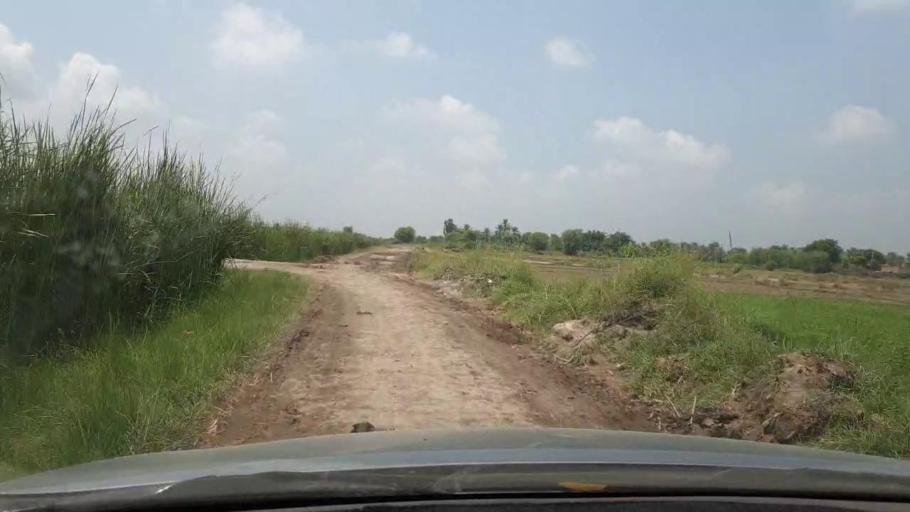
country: PK
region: Sindh
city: Khairpur
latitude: 27.4724
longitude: 68.6842
